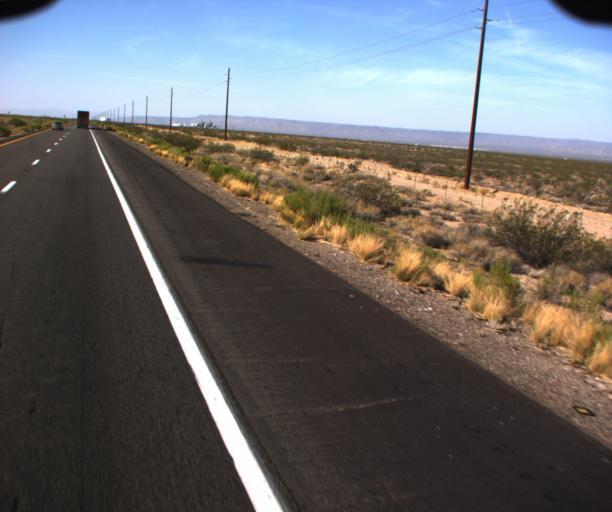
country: US
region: Arizona
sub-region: Mohave County
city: Kingman
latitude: 35.0808
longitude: -114.1220
